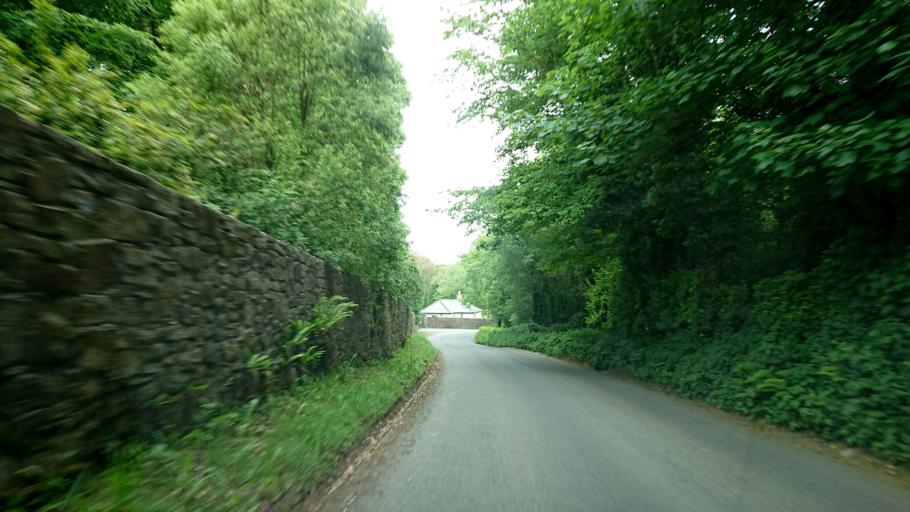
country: IE
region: Munster
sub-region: Waterford
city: Waterford
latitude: 52.2318
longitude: -7.0331
